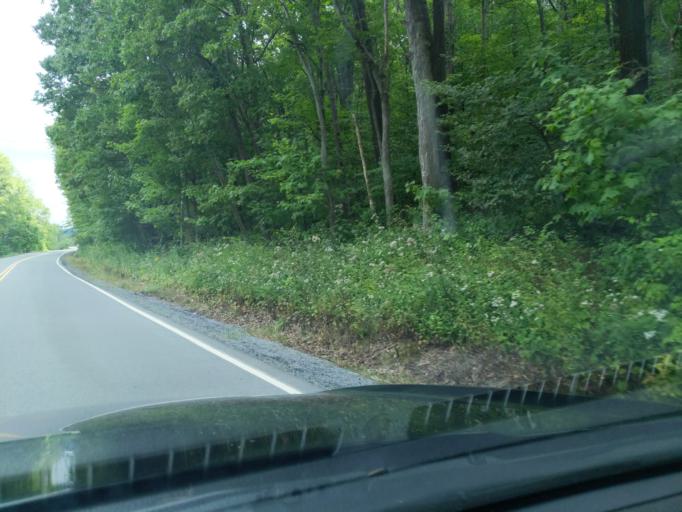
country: US
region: Pennsylvania
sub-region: Cambria County
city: Beaverdale
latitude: 40.2964
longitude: -78.5786
